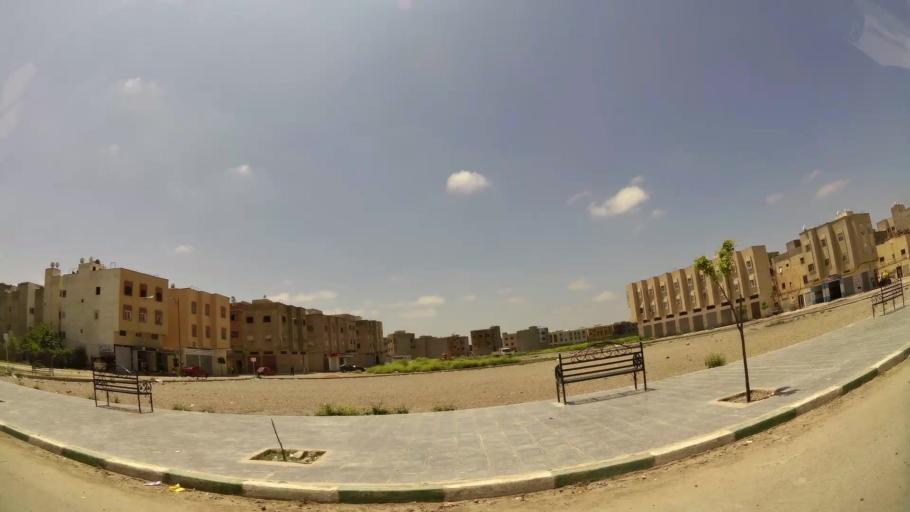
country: MA
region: Fes-Boulemane
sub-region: Fes
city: Fes
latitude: 34.0333
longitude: -5.0473
